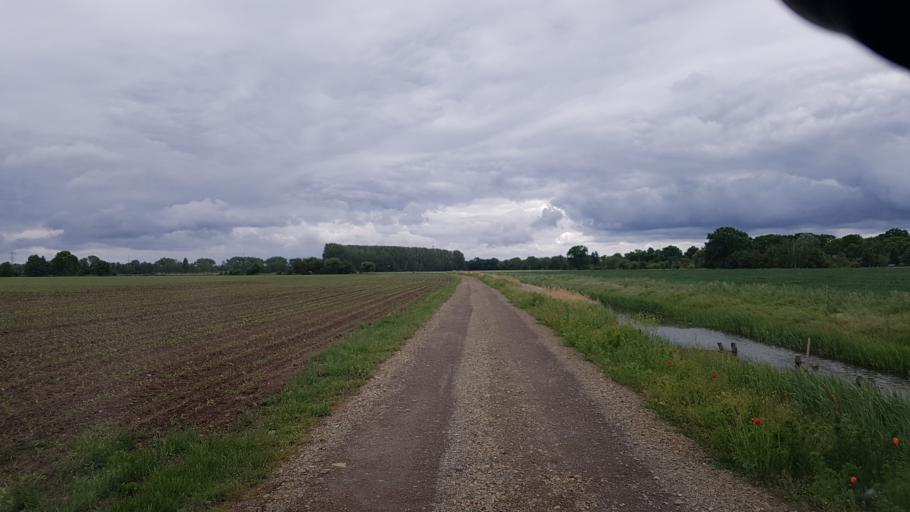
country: DE
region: Brandenburg
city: Doberlug-Kirchhain
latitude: 51.6557
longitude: 13.5476
